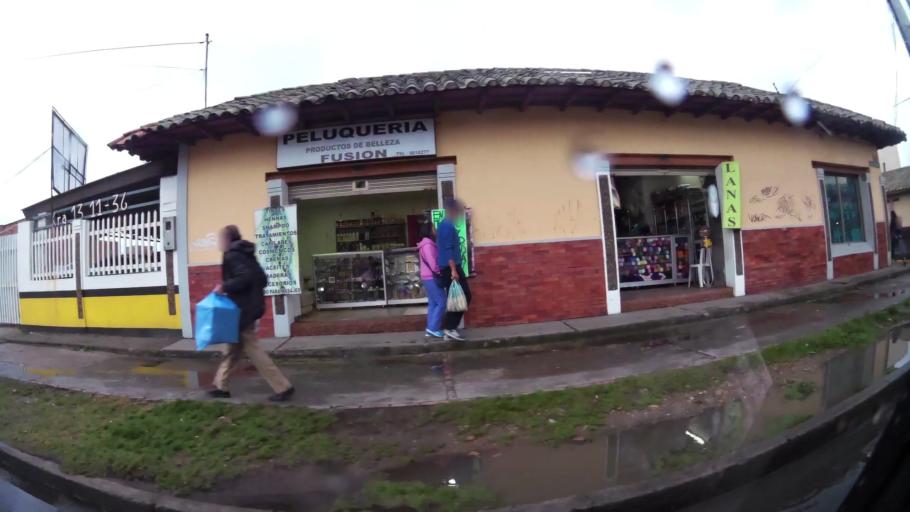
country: CO
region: Cundinamarca
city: Chia
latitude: 4.8619
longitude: -74.0621
